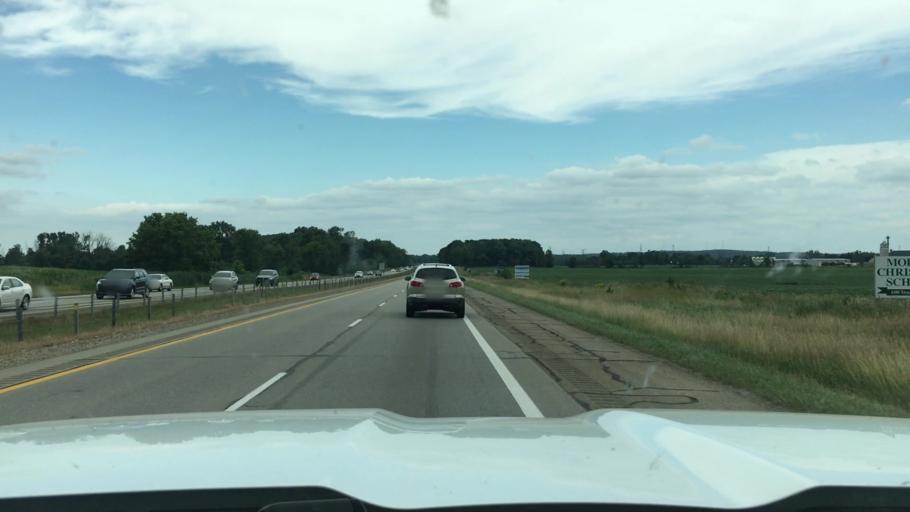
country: US
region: Michigan
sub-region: Allegan County
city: Wayland
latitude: 42.7400
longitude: -85.6732
